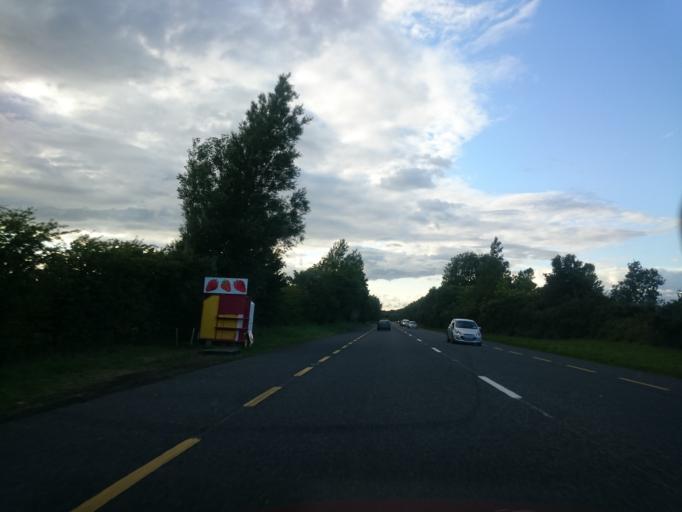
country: IE
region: Leinster
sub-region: Loch Garman
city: Loch Garman
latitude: 52.3689
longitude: -6.5161
